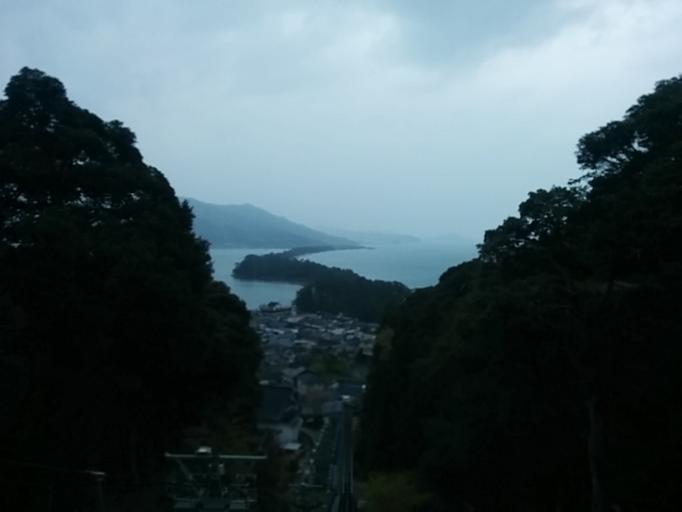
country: JP
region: Kyoto
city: Miyazu
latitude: 35.5543
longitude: 135.1830
